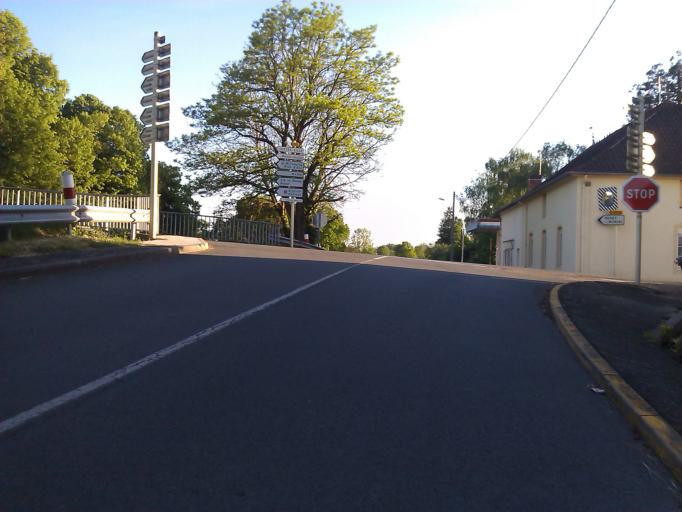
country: FR
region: Bourgogne
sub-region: Departement de Saone-et-Loire
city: Palinges
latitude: 46.5548
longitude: 4.2149
